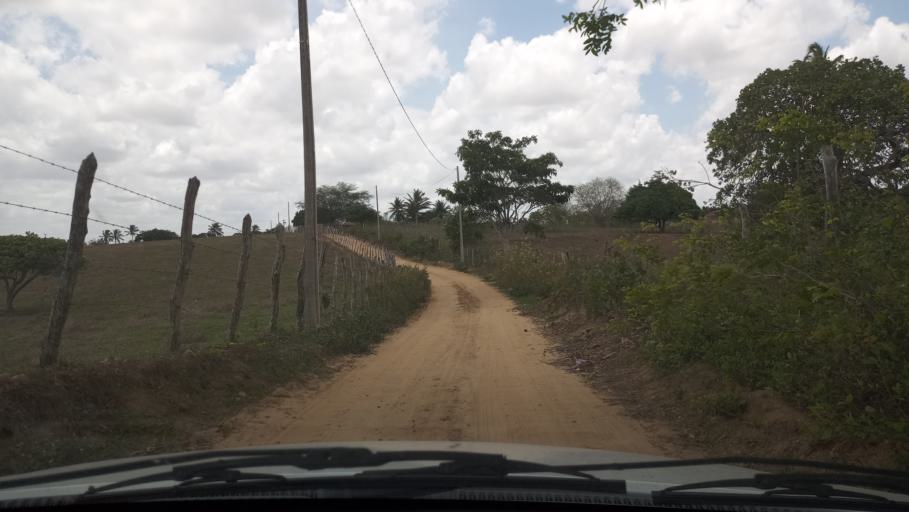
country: BR
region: Rio Grande do Norte
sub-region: Brejinho
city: Brejinho
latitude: -6.2731
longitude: -35.3443
